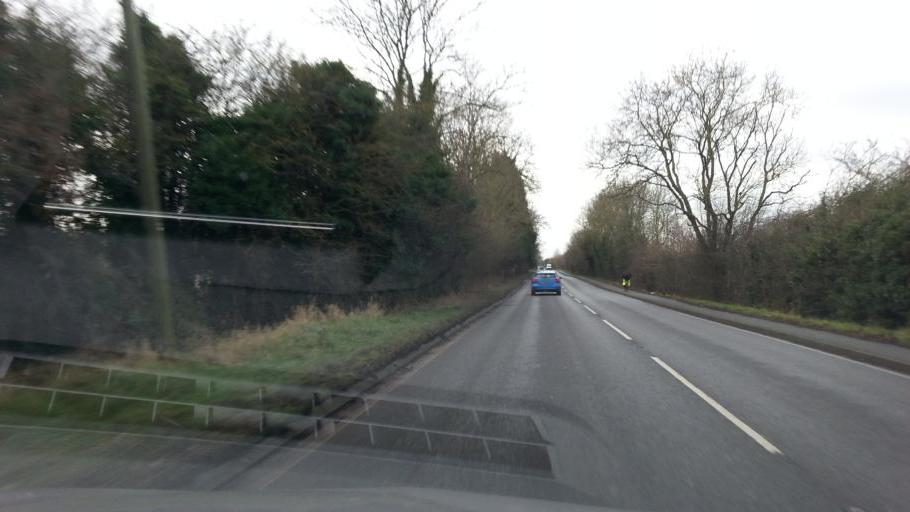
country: GB
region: England
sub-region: Leicestershire
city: Castle Donington
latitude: 52.8684
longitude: -1.3108
